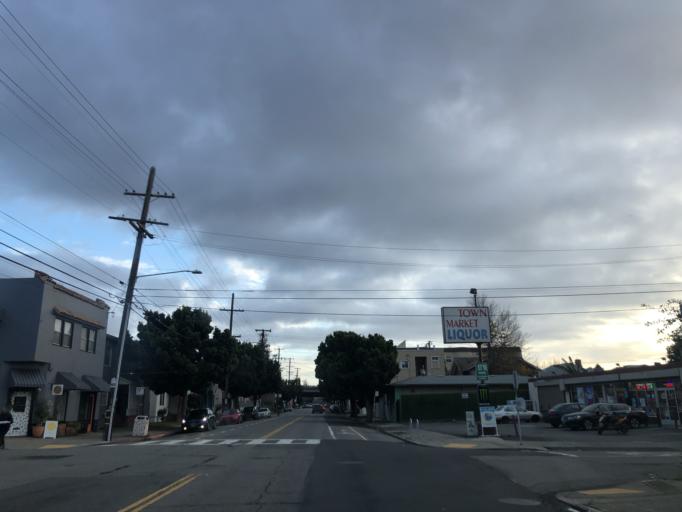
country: US
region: California
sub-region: Alameda County
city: Emeryville
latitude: 37.8423
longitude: -122.2648
